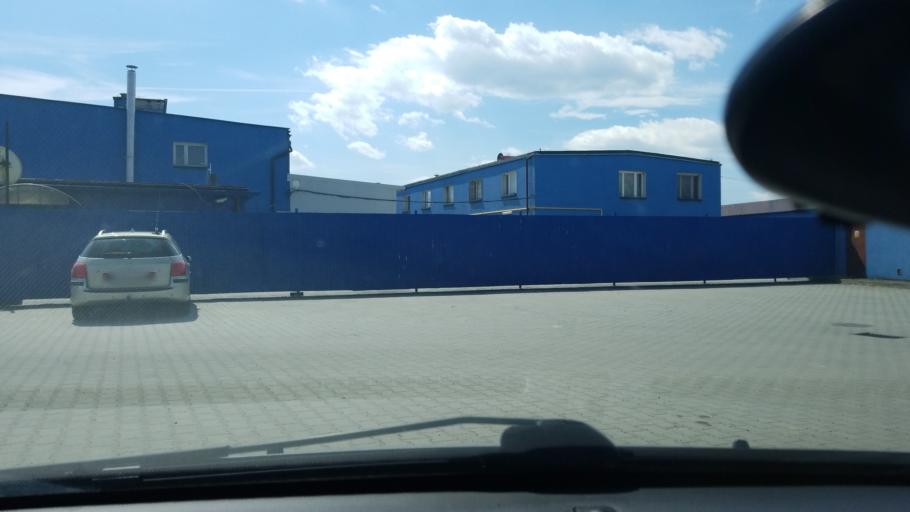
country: PL
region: Subcarpathian Voivodeship
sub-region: Powiat jasielski
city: Jaslo
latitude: 49.7312
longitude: 21.4605
